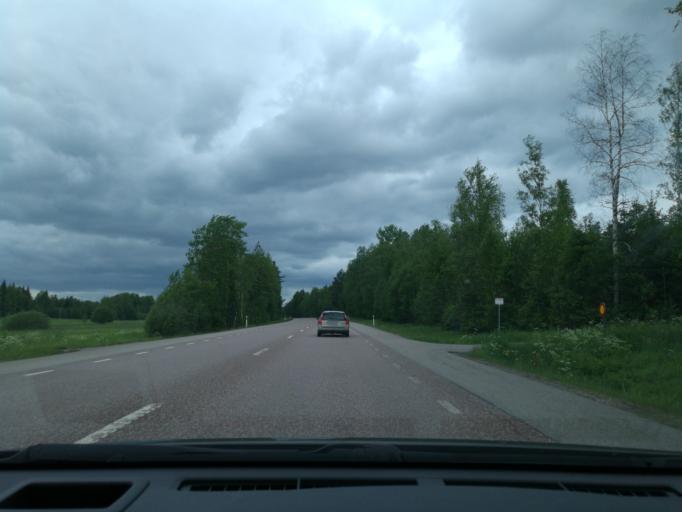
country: SE
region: Dalarna
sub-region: Smedjebackens Kommun
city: Smedjebacken
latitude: 60.0603
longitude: 15.5553
